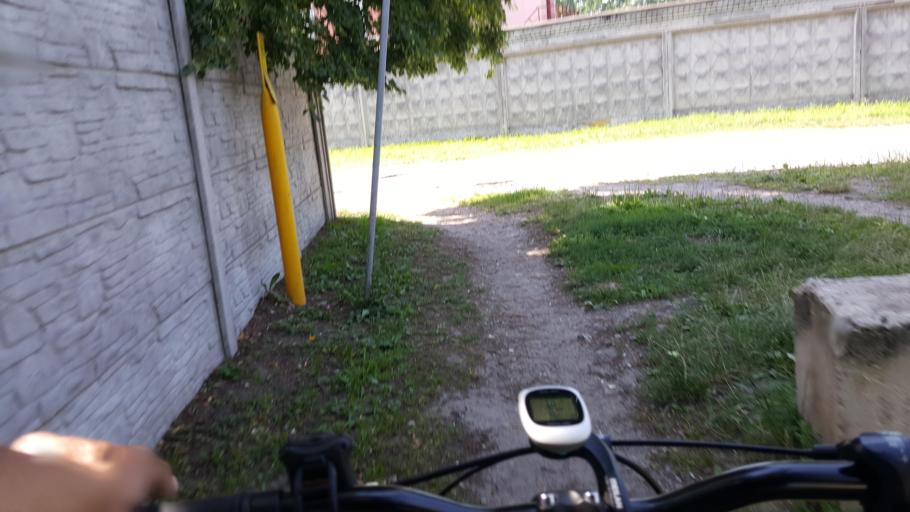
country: BY
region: Brest
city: Zhabinka
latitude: 52.2017
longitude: 24.0209
